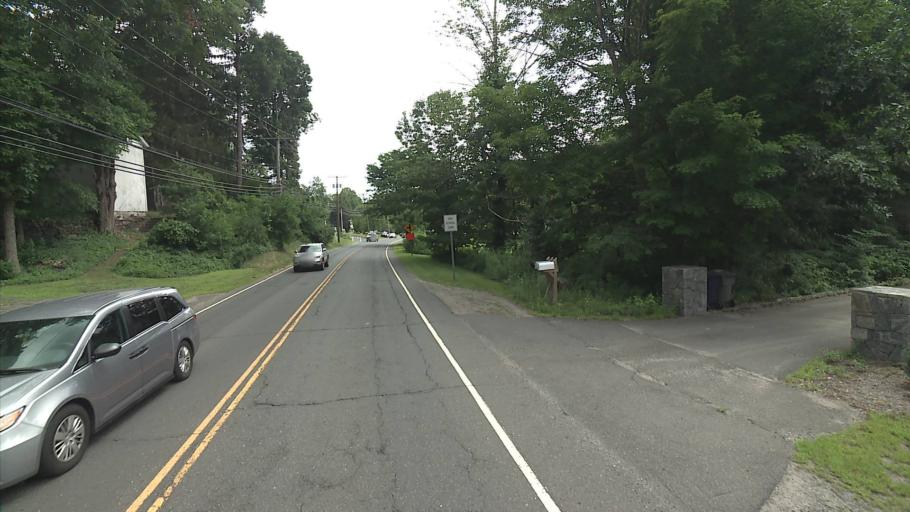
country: US
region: Connecticut
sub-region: New Haven County
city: Oxford
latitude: 41.4361
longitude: -73.1187
